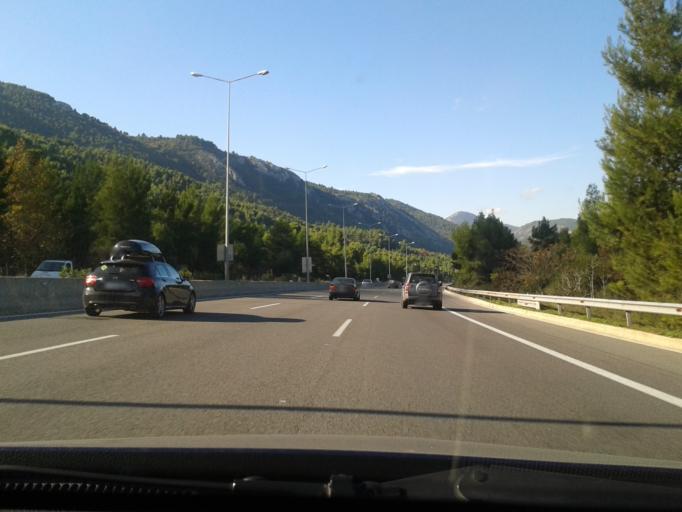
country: GR
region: Attica
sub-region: Nomarchia Anatolikis Attikis
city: Afidnes
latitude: 38.2294
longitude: 23.8279
